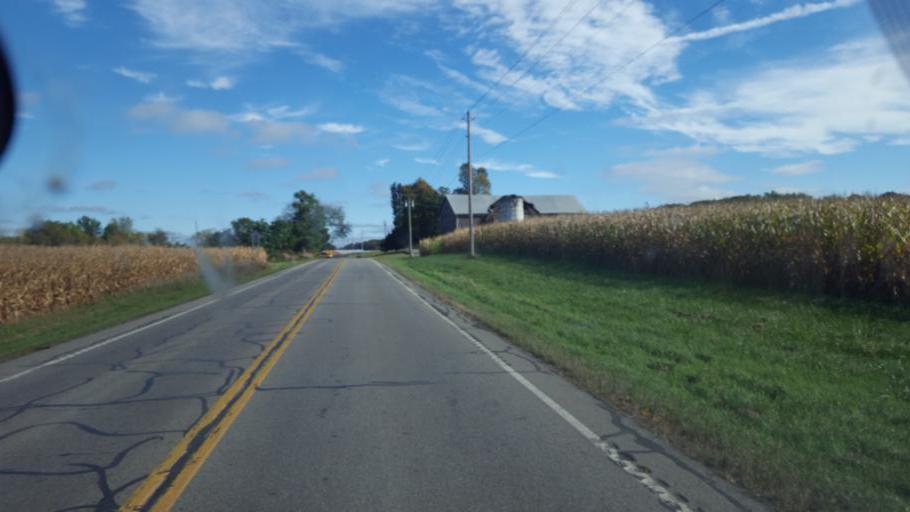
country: US
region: Ohio
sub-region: Richland County
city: Lincoln Heights
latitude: 40.8978
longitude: -82.5032
